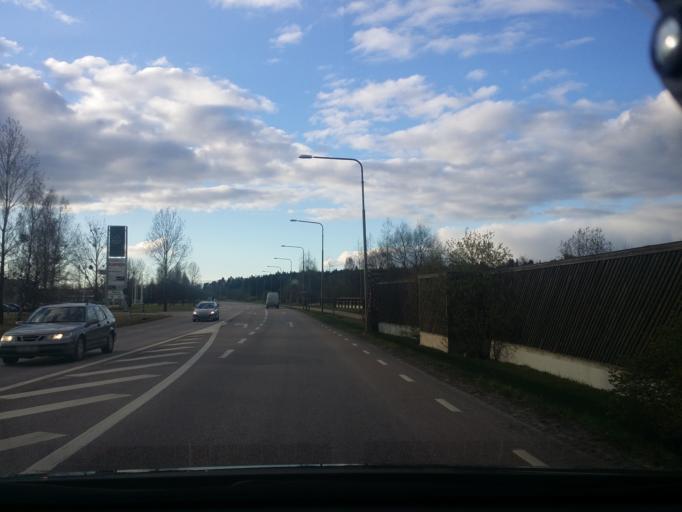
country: SE
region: Vaestmanland
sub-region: Vasteras
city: Vasteras
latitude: 59.5979
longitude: 16.4978
